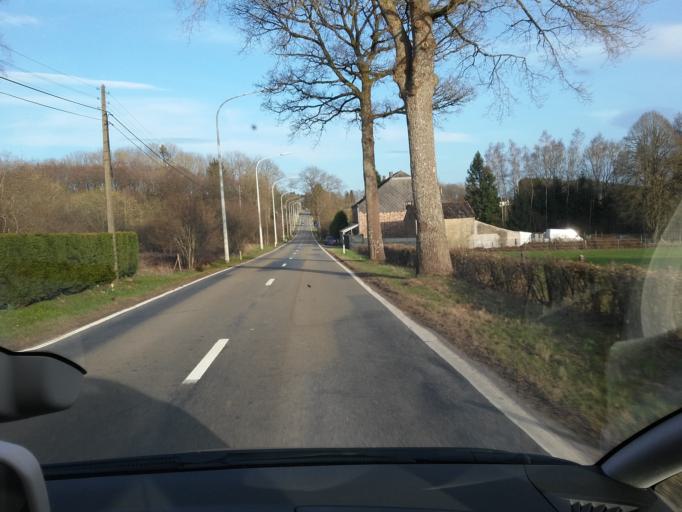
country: BE
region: Wallonia
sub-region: Province du Luxembourg
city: Libin
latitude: 50.0100
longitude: 5.2057
